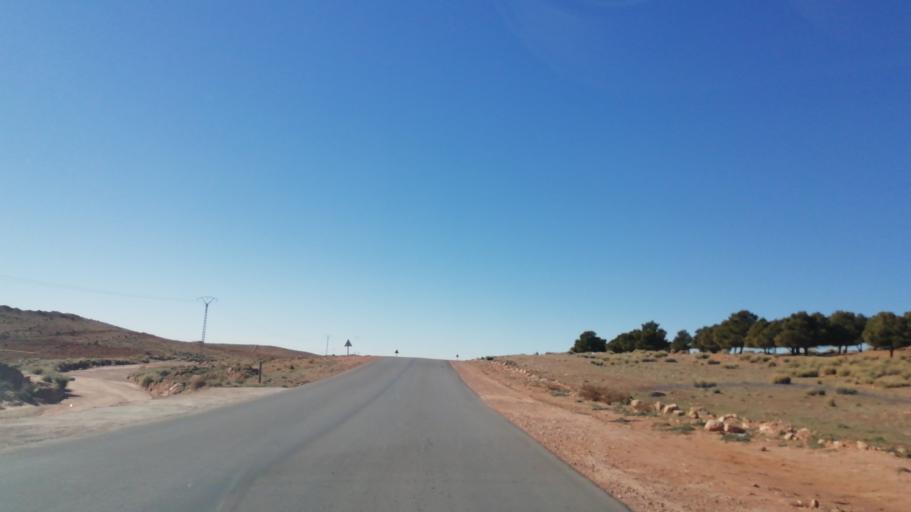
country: DZ
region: El Bayadh
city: El Bayadh
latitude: 33.6471
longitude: 1.3992
